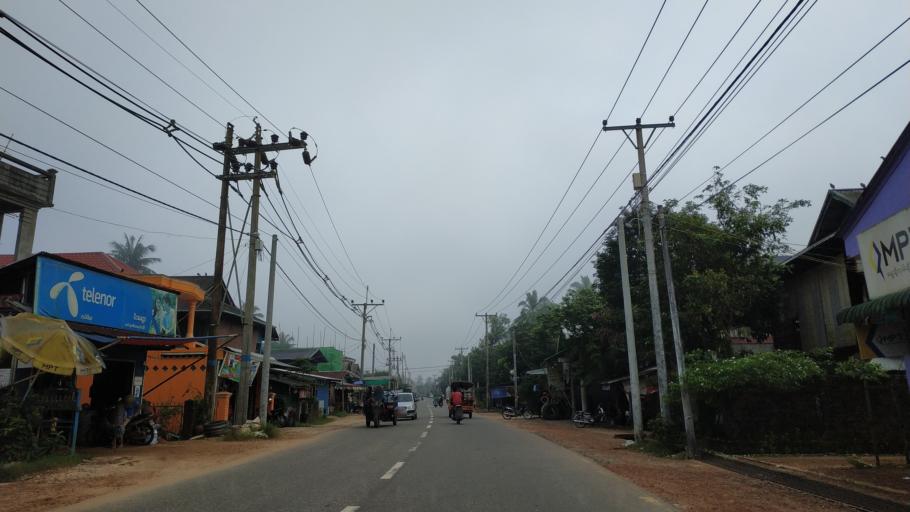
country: MM
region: Tanintharyi
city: Dawei
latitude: 14.0983
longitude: 98.1958
